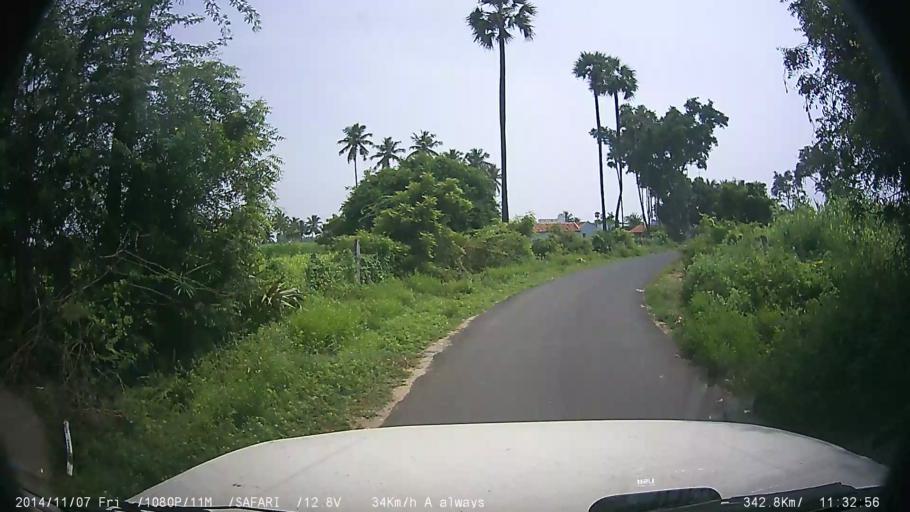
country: IN
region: Tamil Nadu
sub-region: Tiruppur
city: Avinashi
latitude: 11.1647
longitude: 77.2749
